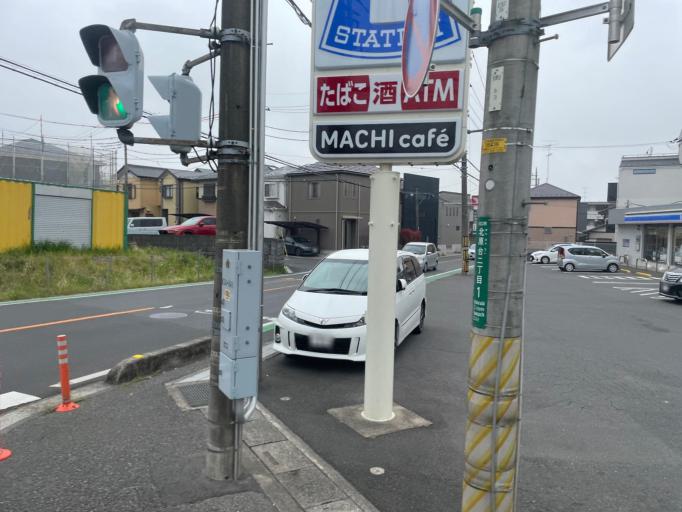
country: JP
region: Saitama
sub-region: Kawaguchi-shi
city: Hatogaya-honcho
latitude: 35.8677
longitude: 139.7411
